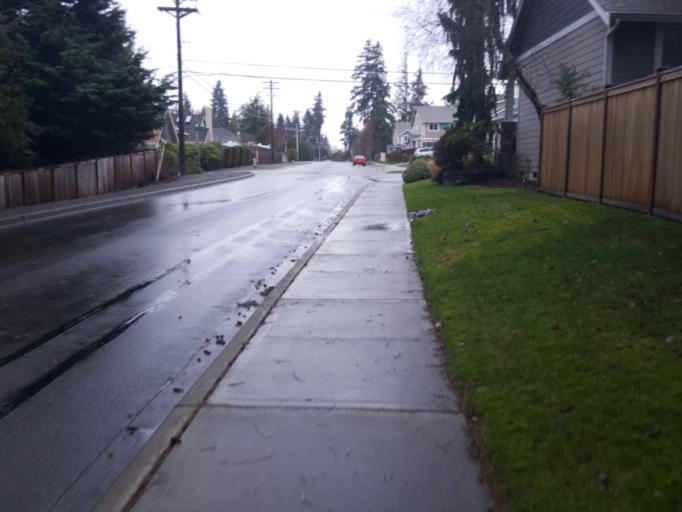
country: US
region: Washington
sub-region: Pierce County
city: University Place
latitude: 47.2094
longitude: -122.5372
